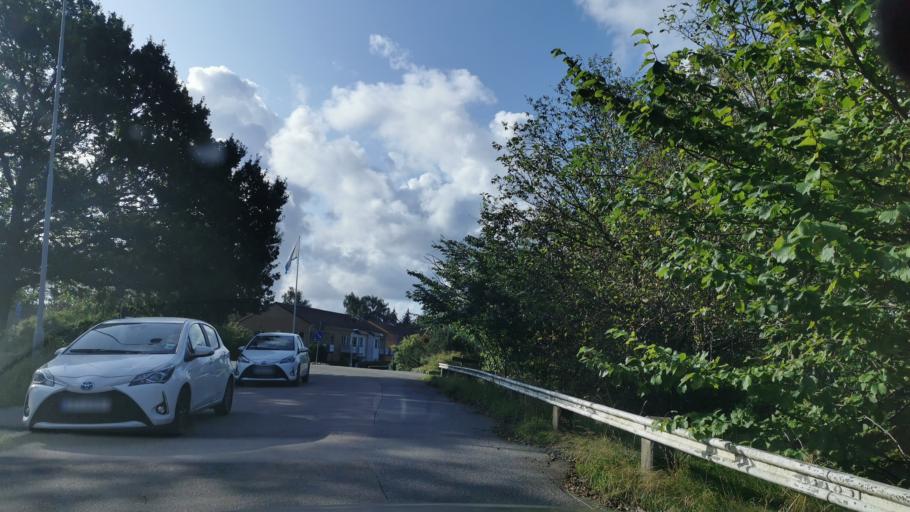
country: SE
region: Vaestra Goetaland
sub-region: Goteborg
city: Majorna
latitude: 57.6488
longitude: 11.9205
